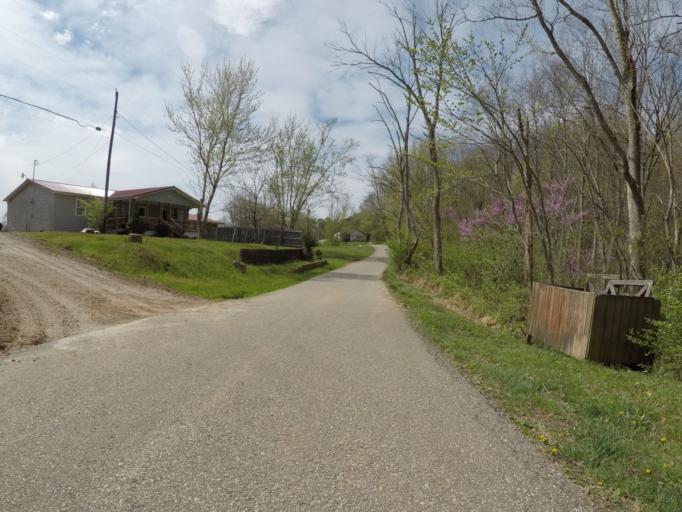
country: US
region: West Virginia
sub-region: Wayne County
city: Lavalette
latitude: 38.3428
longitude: -82.3686
